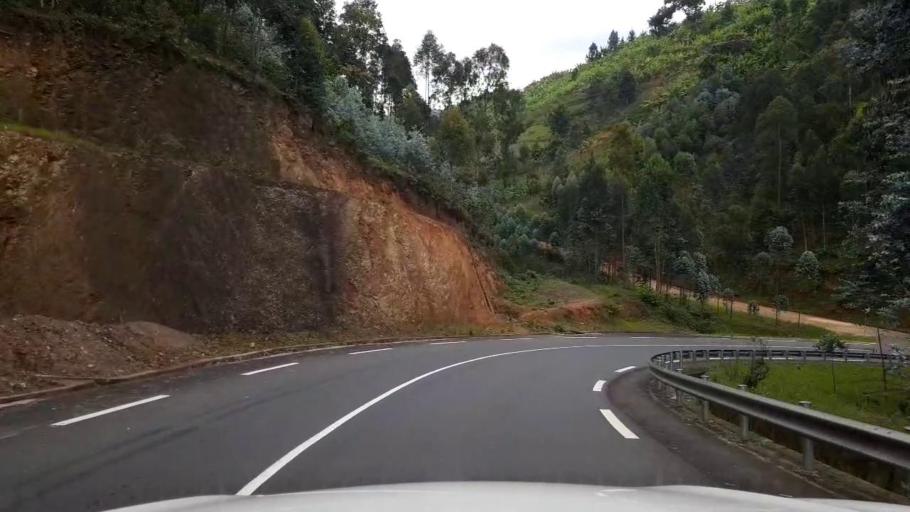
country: RW
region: Western Province
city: Kibuye
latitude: -1.9034
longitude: 29.3597
